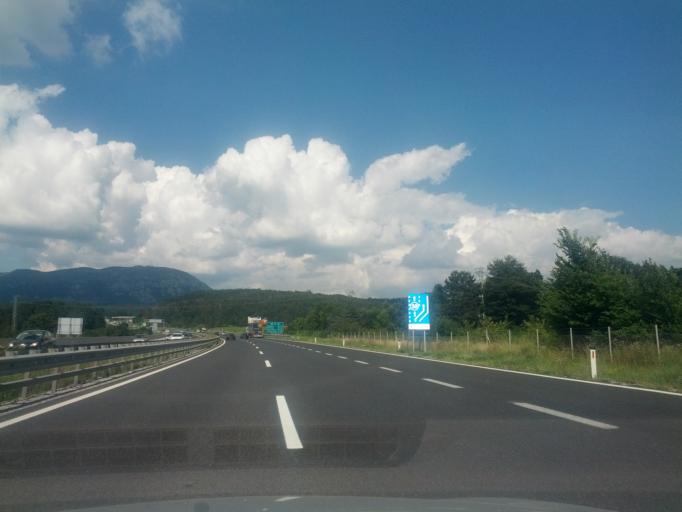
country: SI
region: Divaca
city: Divaca
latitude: 45.7249
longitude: 14.0141
